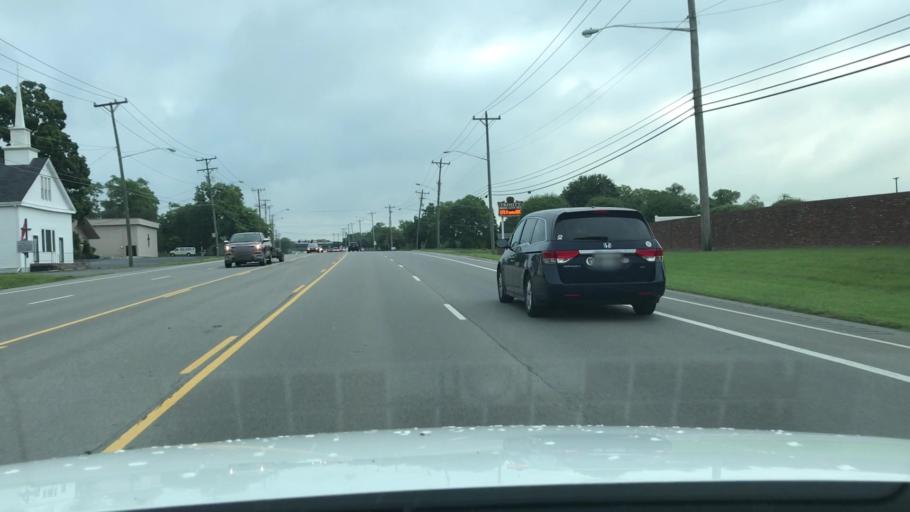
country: US
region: Tennessee
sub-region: Sumner County
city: Hendersonville
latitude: 36.3248
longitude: -86.5662
